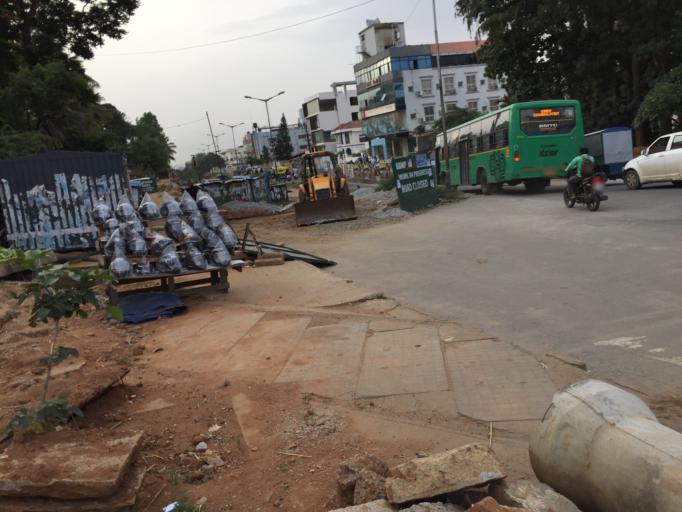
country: IN
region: Karnataka
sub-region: Bangalore Urban
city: Bangalore
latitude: 12.9292
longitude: 77.5448
